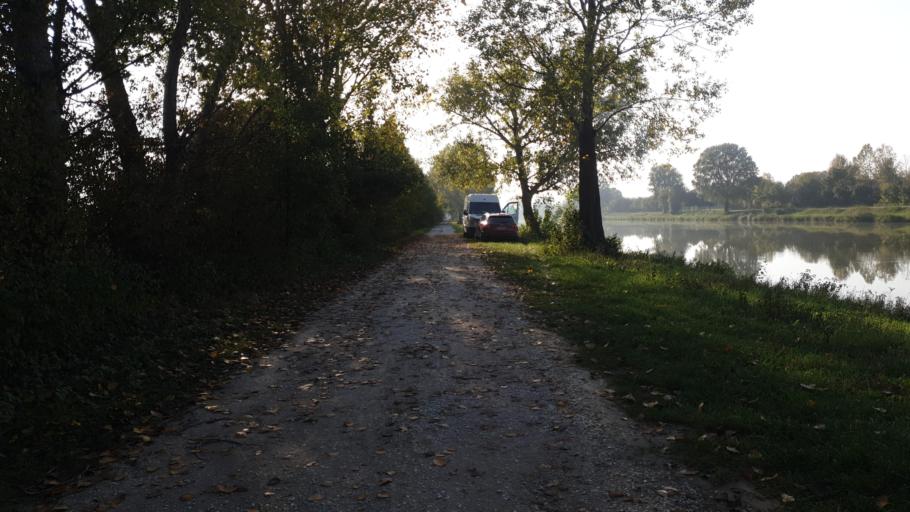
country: IT
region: Veneto
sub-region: Provincia di Venezia
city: Tombelle
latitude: 45.3880
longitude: 11.9916
